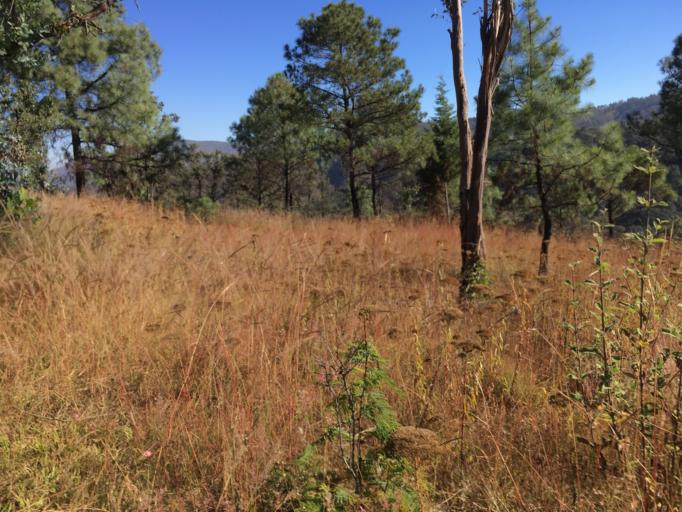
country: MX
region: Michoacan
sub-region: Morelia
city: Montana Monarca (Punta Altozano)
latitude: 19.6641
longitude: -101.1446
